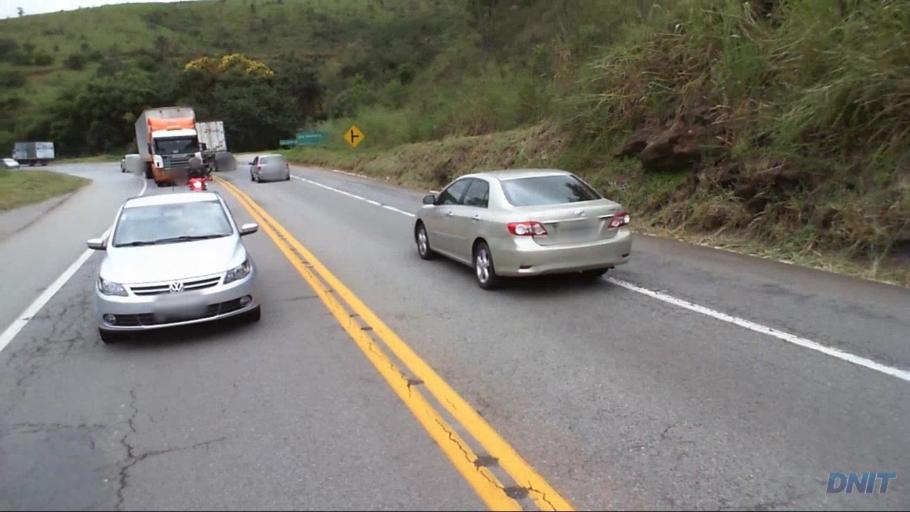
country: BR
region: Minas Gerais
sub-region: Joao Monlevade
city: Joao Monlevade
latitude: -19.8540
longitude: -43.2578
